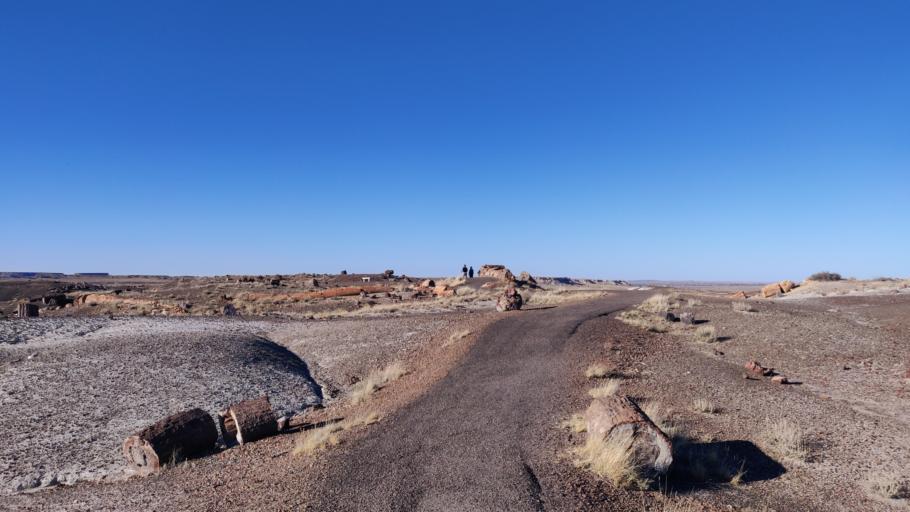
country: US
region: Arizona
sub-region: Navajo County
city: Holbrook
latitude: 34.8662
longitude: -109.7885
